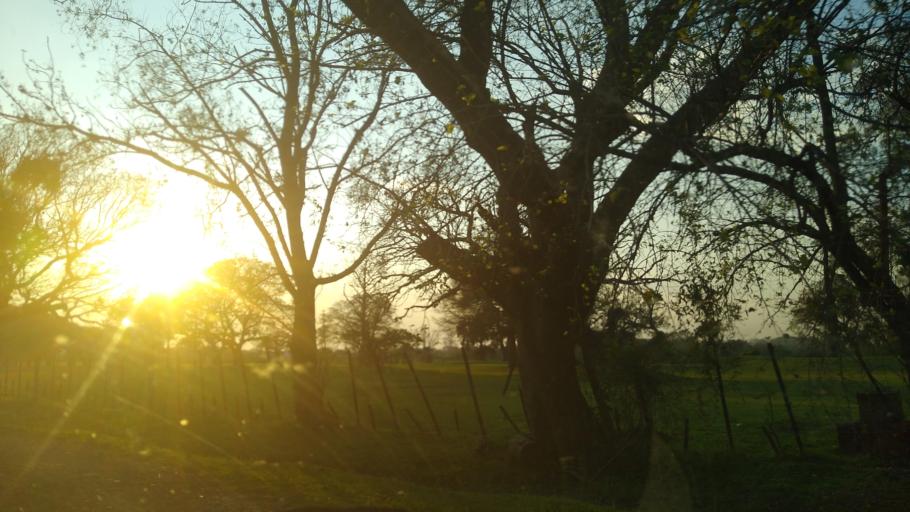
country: AR
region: Chaco
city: Barranqueras
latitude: -27.4699
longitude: -58.9545
